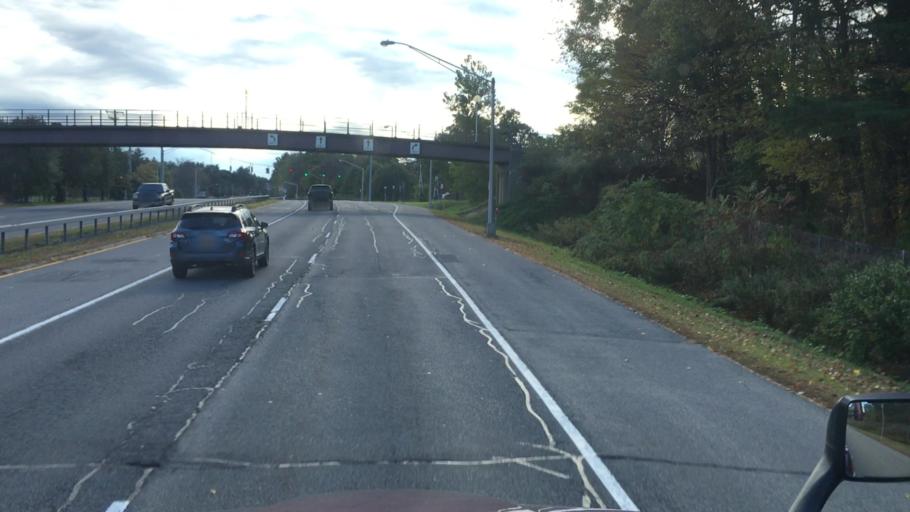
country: US
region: New York
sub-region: Saratoga County
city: Saratoga Springs
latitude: 43.0559
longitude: -73.8095
